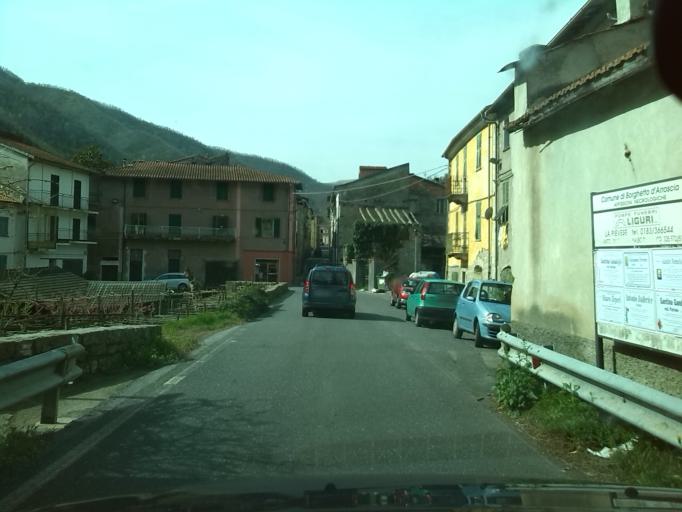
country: IT
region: Liguria
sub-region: Provincia di Imperia
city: Borghetto d'Arroscia
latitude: 44.0588
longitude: 7.9830
